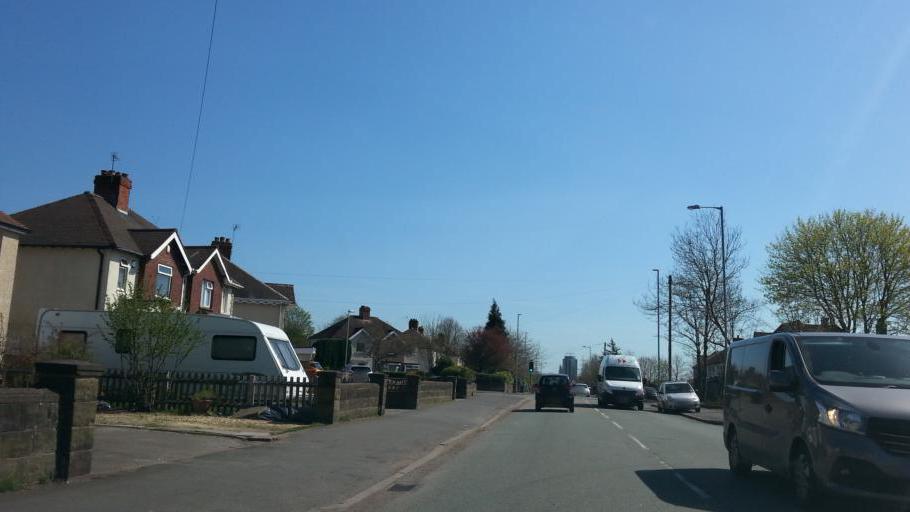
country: GB
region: England
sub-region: Staffordshire
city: Cannock
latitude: 52.6814
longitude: -2.0366
